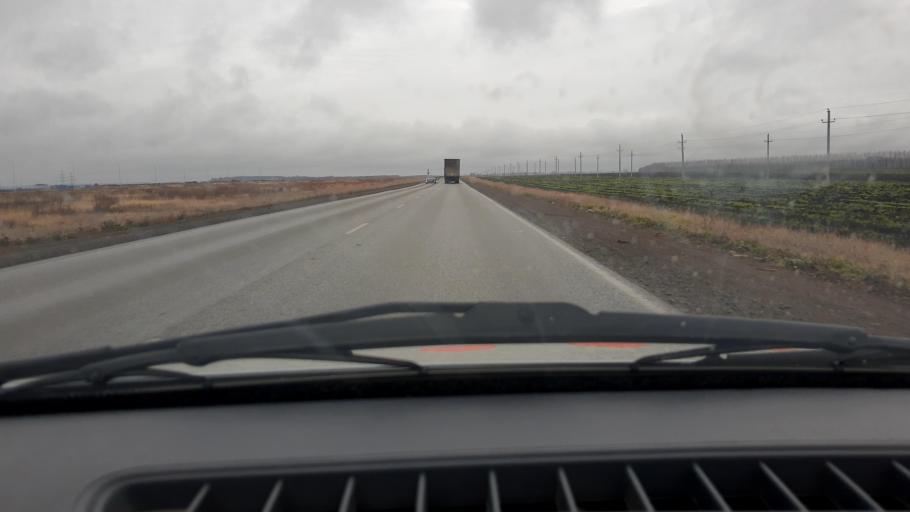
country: RU
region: Bashkortostan
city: Iglino
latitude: 54.7592
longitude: 56.2731
